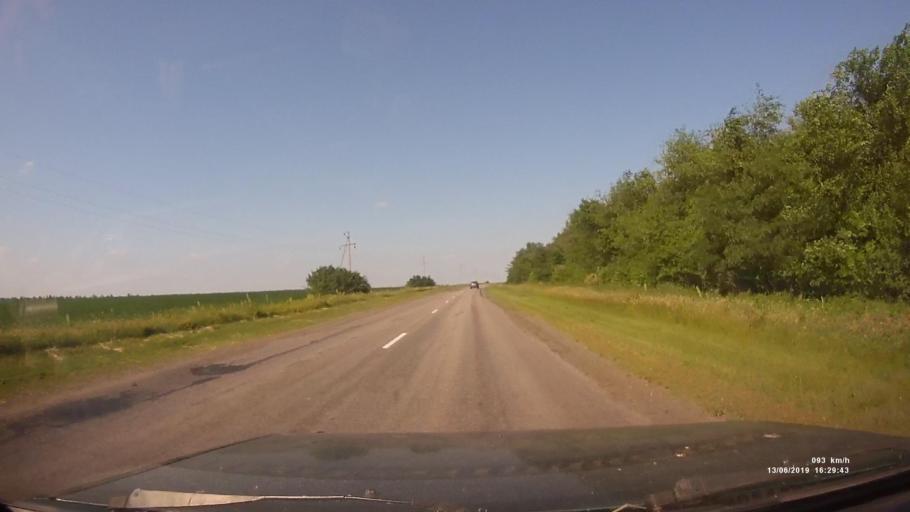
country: RU
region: Rostov
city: Kazanskaya
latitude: 49.8326
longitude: 41.2216
